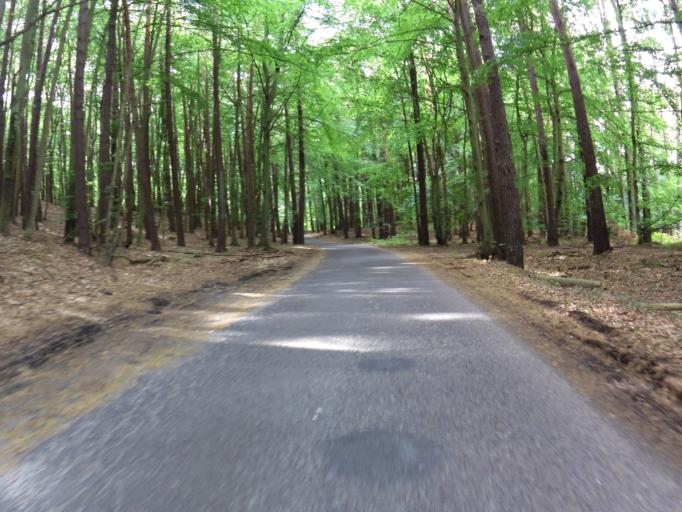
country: DE
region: Mecklenburg-Vorpommern
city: Seebad Bansin
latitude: 53.9795
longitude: 14.1078
